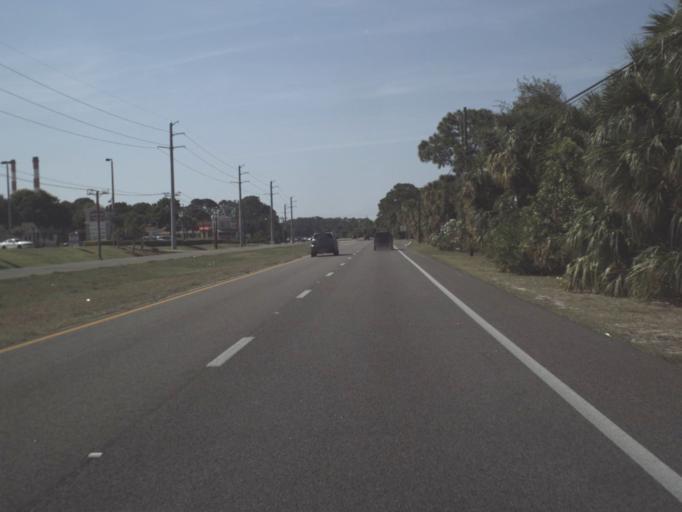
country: US
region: Florida
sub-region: Brevard County
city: Port Saint John
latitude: 28.4864
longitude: -80.7729
